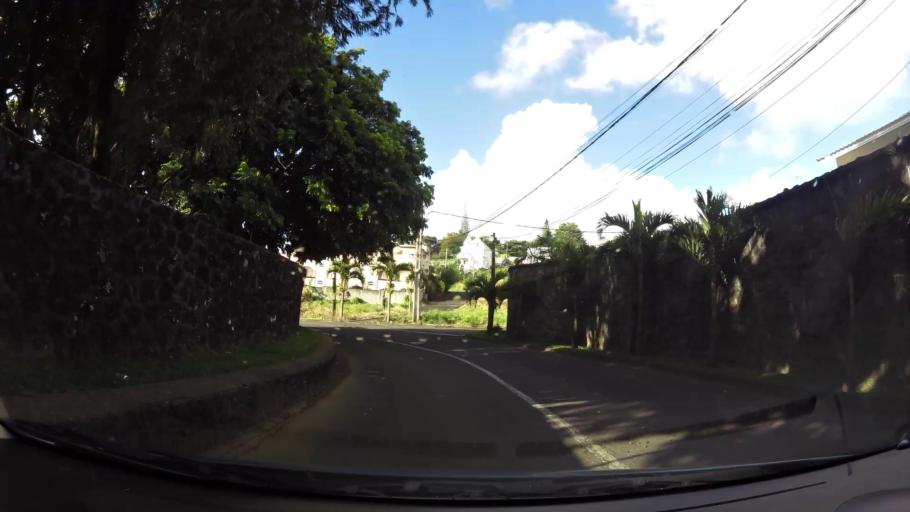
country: MU
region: Plaines Wilhems
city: Vacoas
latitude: -20.3101
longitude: 57.4955
